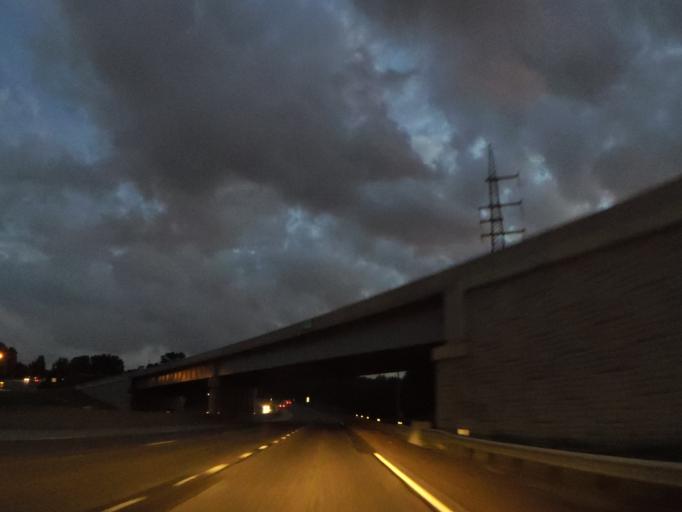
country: US
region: Missouri
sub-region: Saint Louis County
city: Saint George
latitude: 38.5415
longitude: -90.3020
